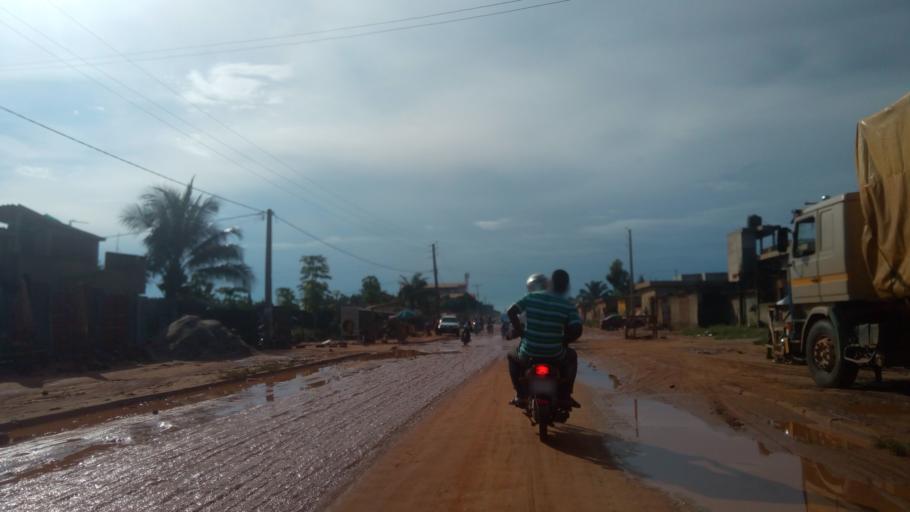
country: BJ
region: Atlantique
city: Abomey-Calavi
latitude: 6.4542
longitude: 2.3340
